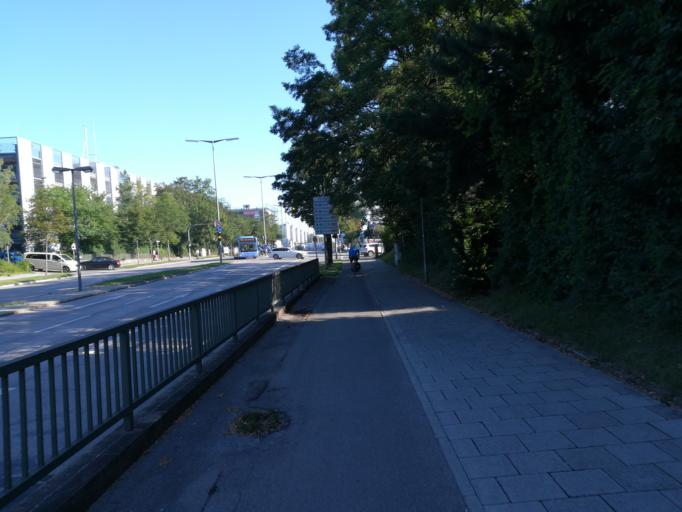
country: DE
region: Bavaria
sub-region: Upper Bavaria
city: Munich
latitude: 48.1908
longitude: 11.5658
